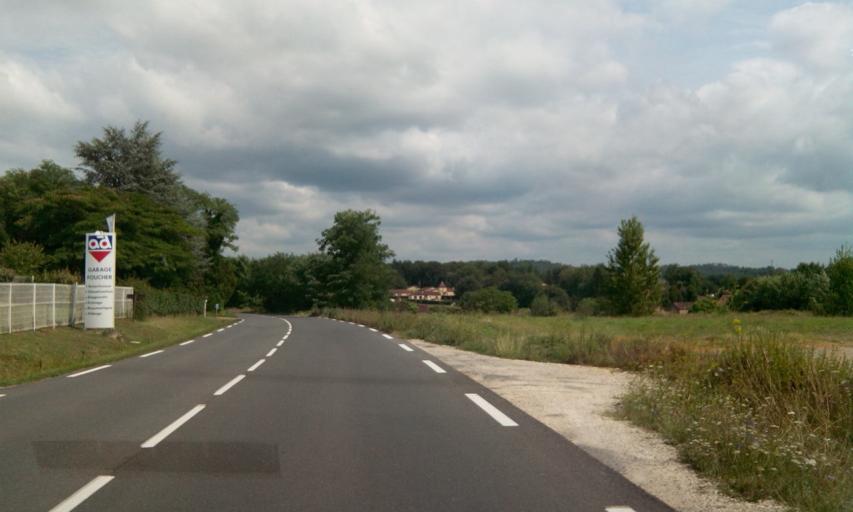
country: FR
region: Aquitaine
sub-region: Departement de la Dordogne
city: Carsac-Aillac
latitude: 44.8633
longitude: 1.2586
